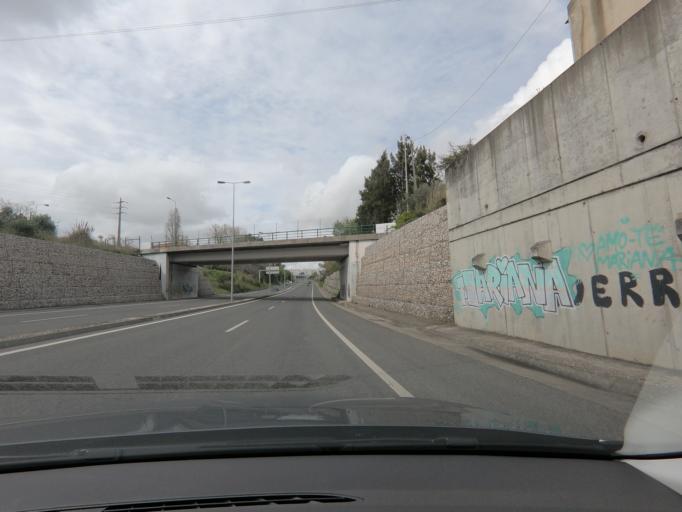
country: PT
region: Lisbon
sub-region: Cascais
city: Sao Domingos de Rana
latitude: 38.6982
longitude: -9.3329
